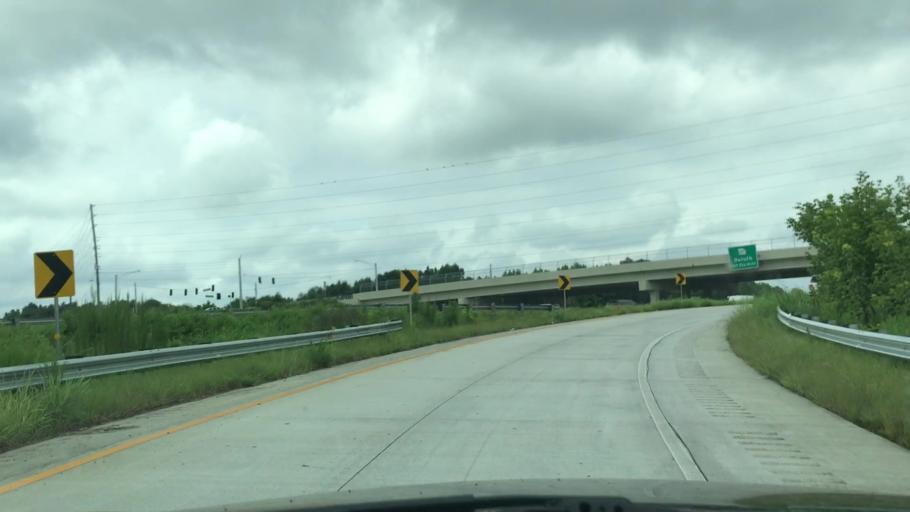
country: US
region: Georgia
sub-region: Gwinnett County
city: Lawrenceville
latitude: 33.9778
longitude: -83.9946
